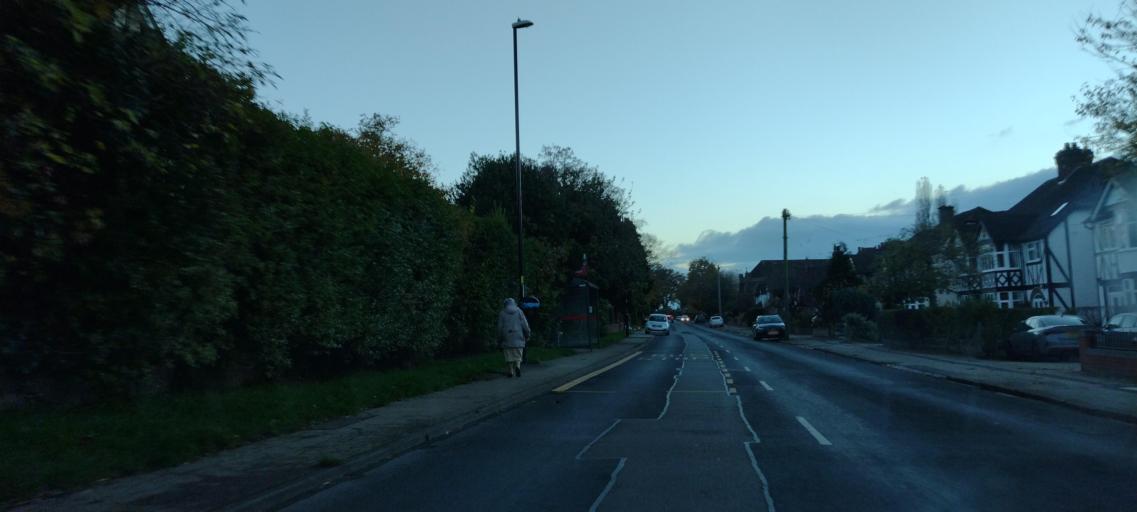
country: GB
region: England
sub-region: Coventry
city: Coventry
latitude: 52.3987
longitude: -1.5379
